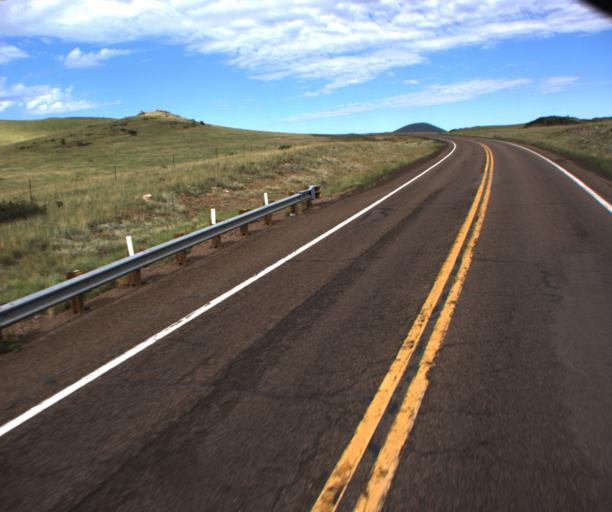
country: US
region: Arizona
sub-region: Apache County
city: Springerville
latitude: 34.2121
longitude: -109.4299
